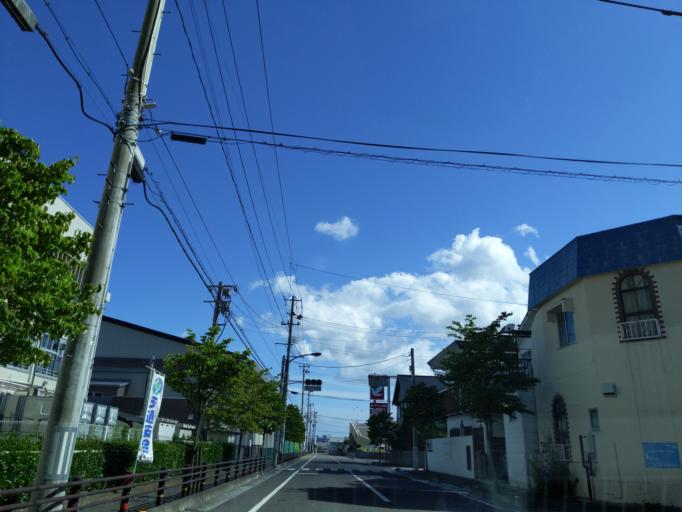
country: JP
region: Fukushima
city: Koriyama
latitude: 37.3921
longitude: 140.3789
